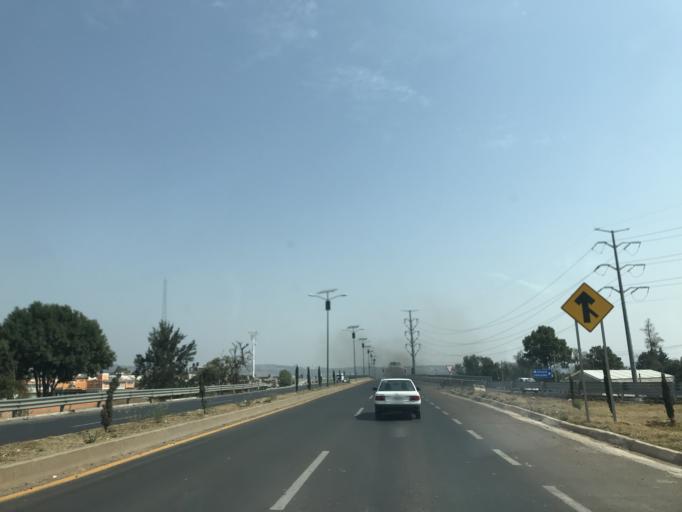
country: MX
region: Tlaxcala
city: Tlaxcala de Xicohtencatl
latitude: 19.3061
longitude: -98.1998
